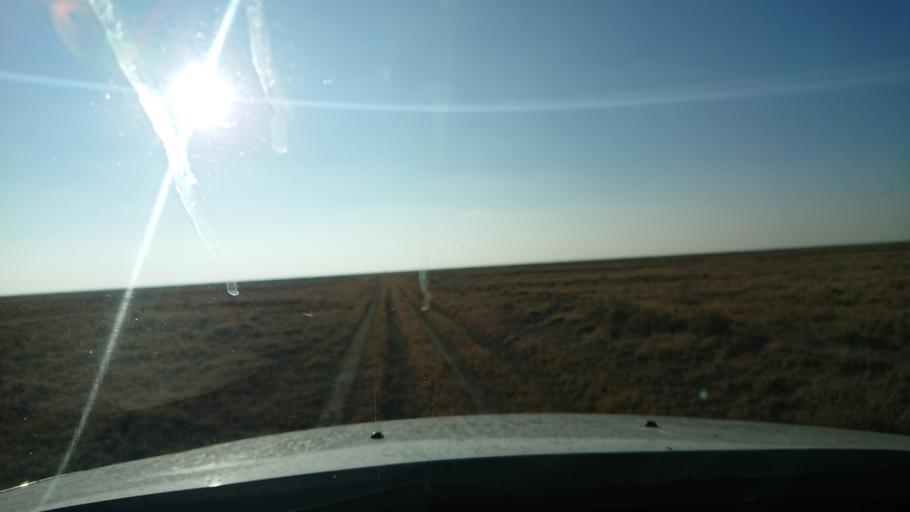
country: TR
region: Aksaray
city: Sultanhani
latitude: 38.3816
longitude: 33.5795
